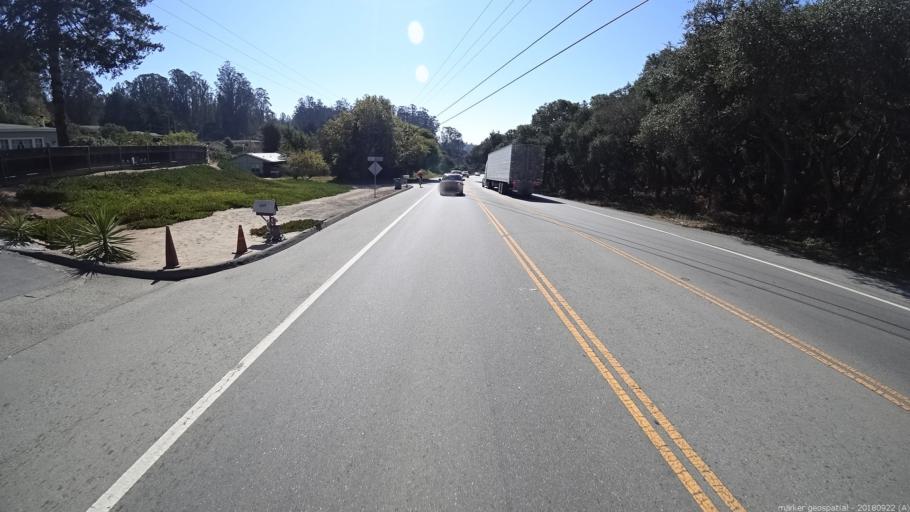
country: US
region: California
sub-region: Monterey County
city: Prunedale
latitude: 36.8297
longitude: -121.6785
